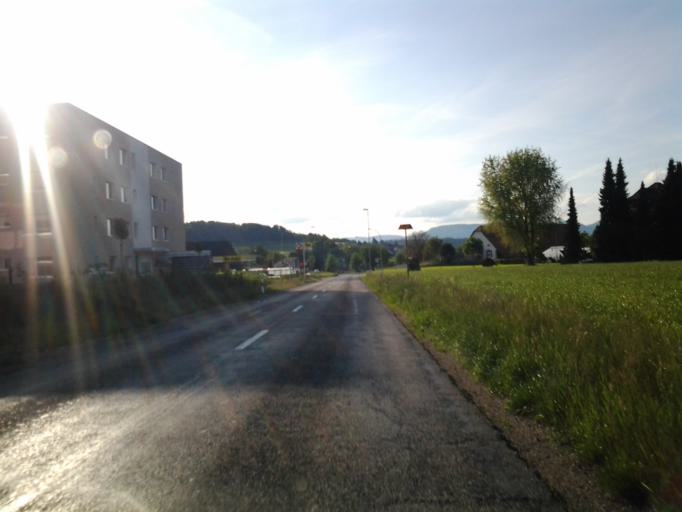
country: CH
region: Bern
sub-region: Oberaargau
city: Roggwil
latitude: 47.2266
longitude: 7.8418
